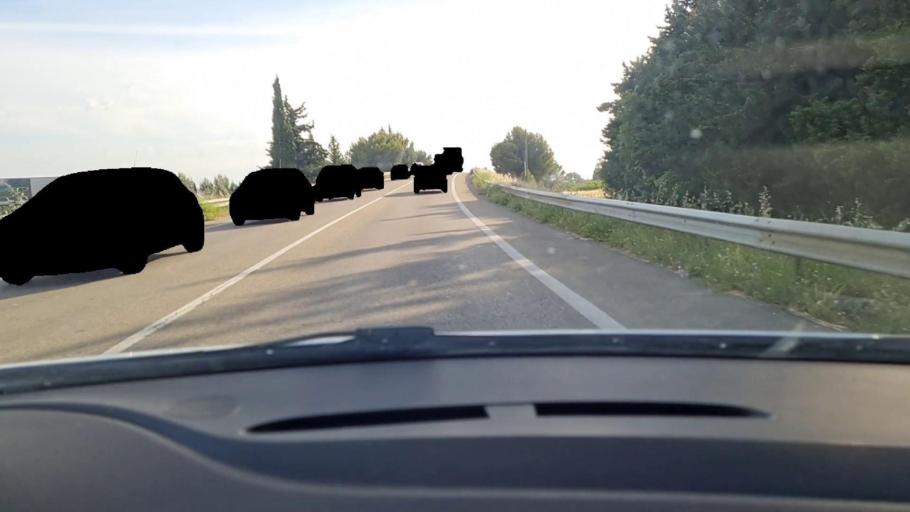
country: FR
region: Languedoc-Roussillon
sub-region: Departement du Gard
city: Caissargues
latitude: 43.7948
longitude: 4.3891
